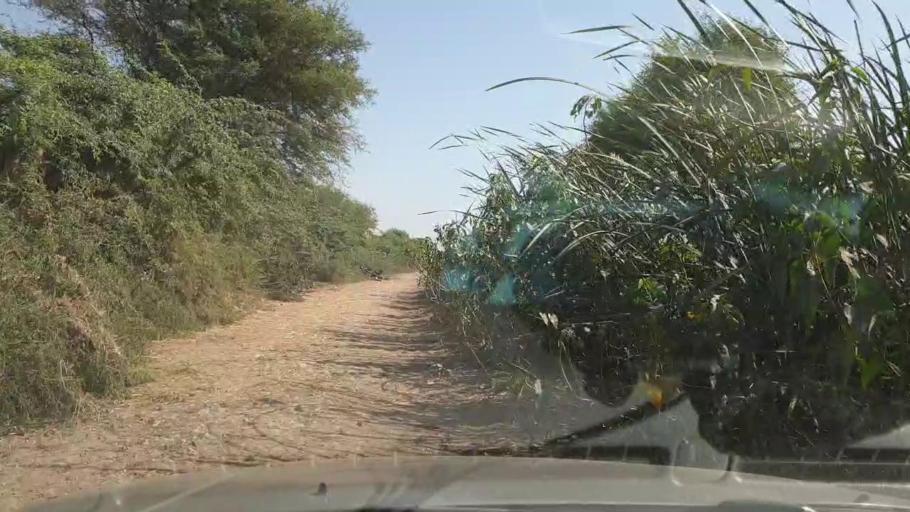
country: PK
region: Sindh
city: Daro Mehar
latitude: 24.9706
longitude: 68.1163
